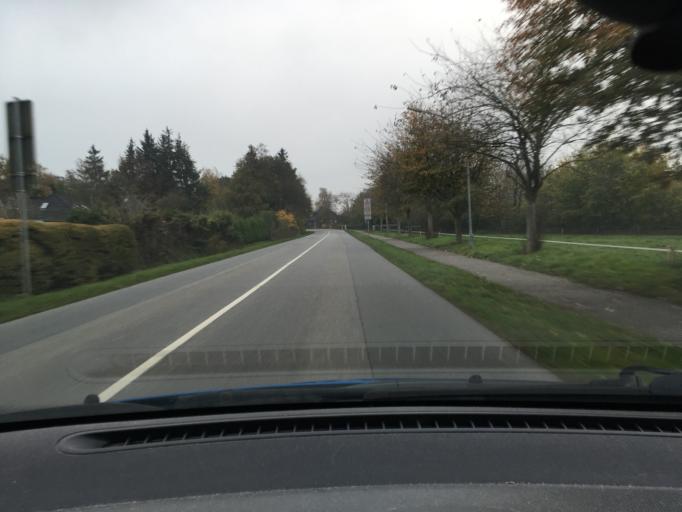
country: DE
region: Schleswig-Holstein
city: Horstedt
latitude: 54.5229
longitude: 9.0682
